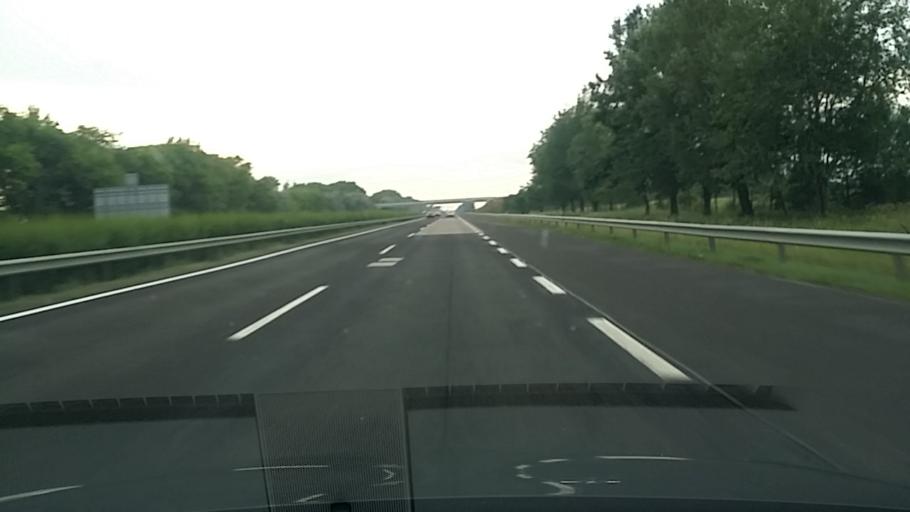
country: HU
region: Heves
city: Fuzesabony
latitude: 47.7306
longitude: 20.4046
